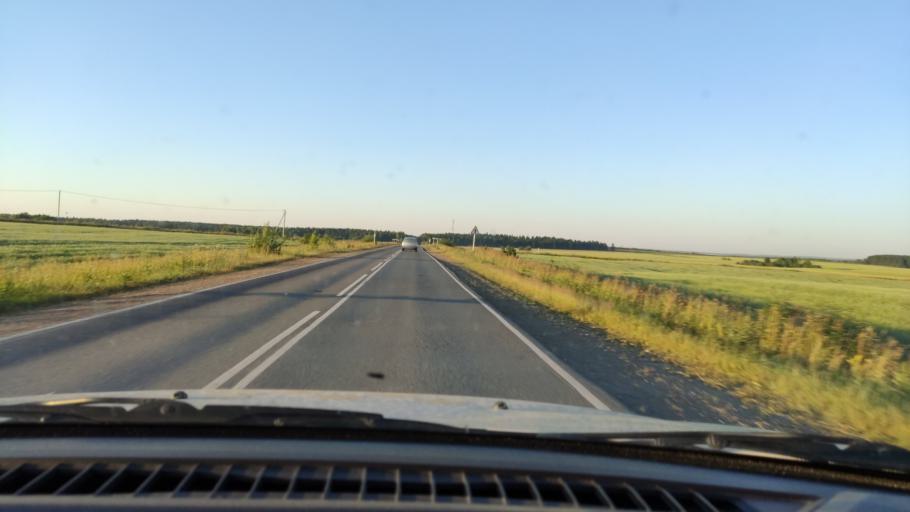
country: RU
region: Perm
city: Kungur
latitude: 57.3858
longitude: 56.8584
